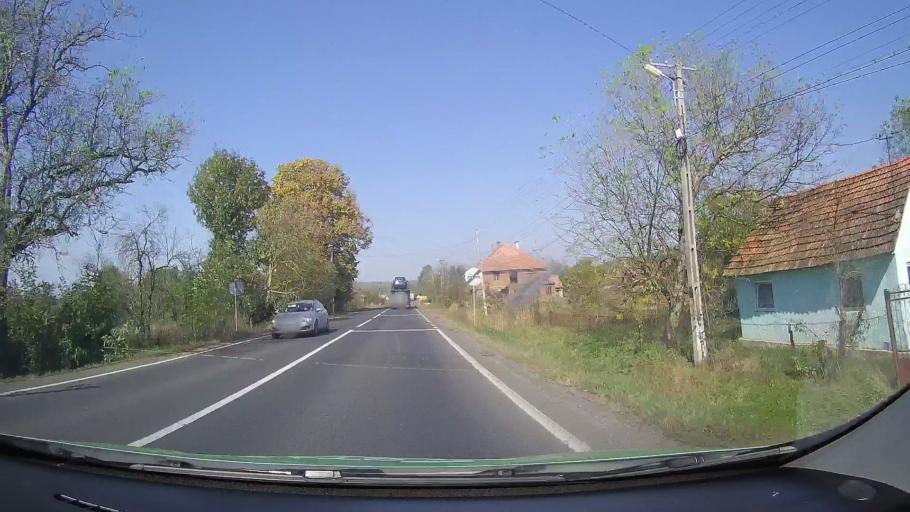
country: RO
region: Arad
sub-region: Comuna Varadia de Mures
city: Varadia de Mures
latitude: 46.0097
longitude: 22.1502
